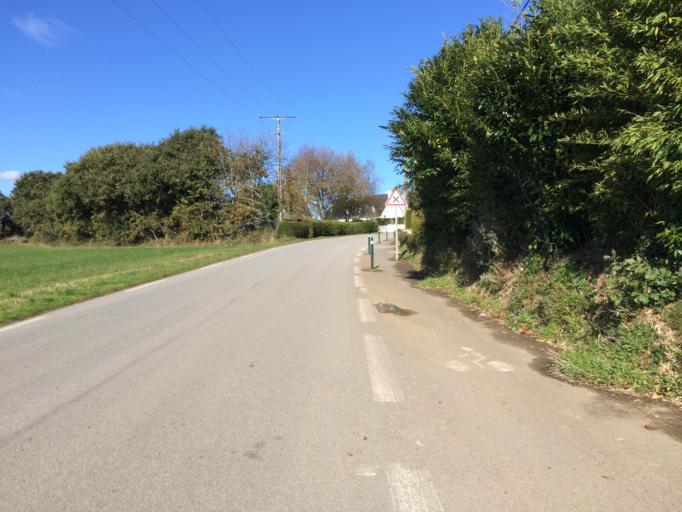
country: FR
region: Brittany
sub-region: Departement du Finistere
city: Saint-Urbain
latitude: 48.3979
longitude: -4.2302
